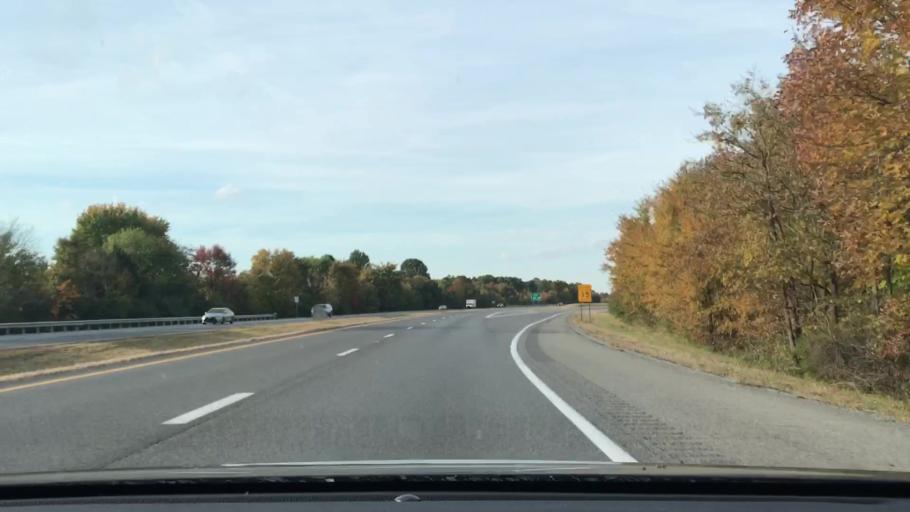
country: US
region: Kentucky
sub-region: Marshall County
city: Benton
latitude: 36.8524
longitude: -88.3711
